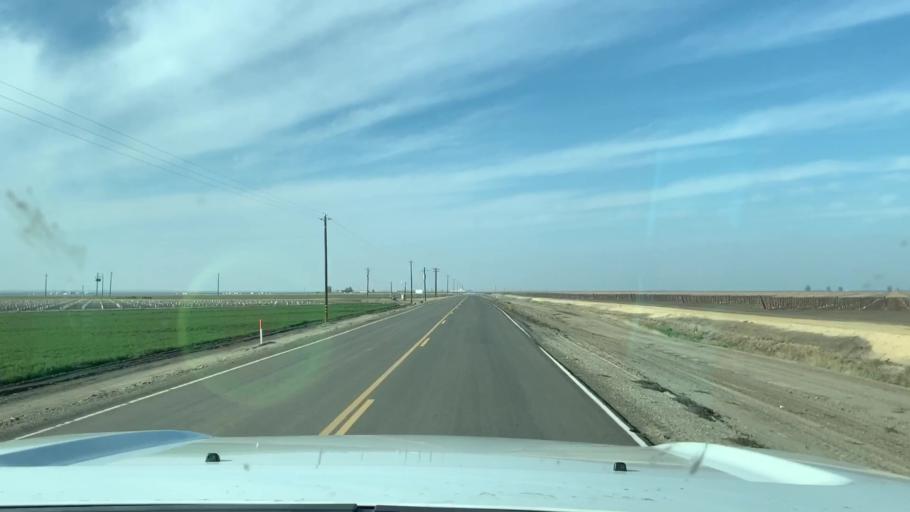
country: US
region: California
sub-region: Kern County
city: Buttonwillow
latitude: 35.4611
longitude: -119.5796
